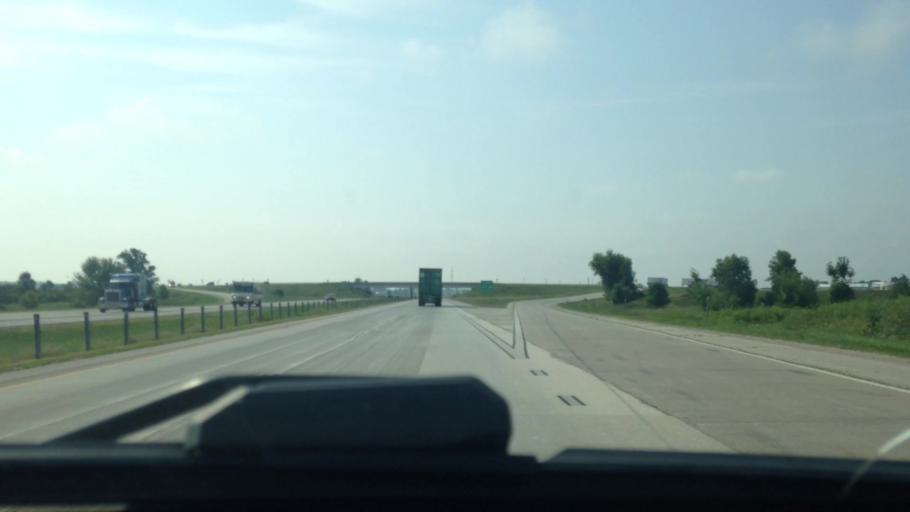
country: US
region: Wisconsin
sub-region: Dodge County
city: Lomira
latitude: 43.6203
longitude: -88.4397
